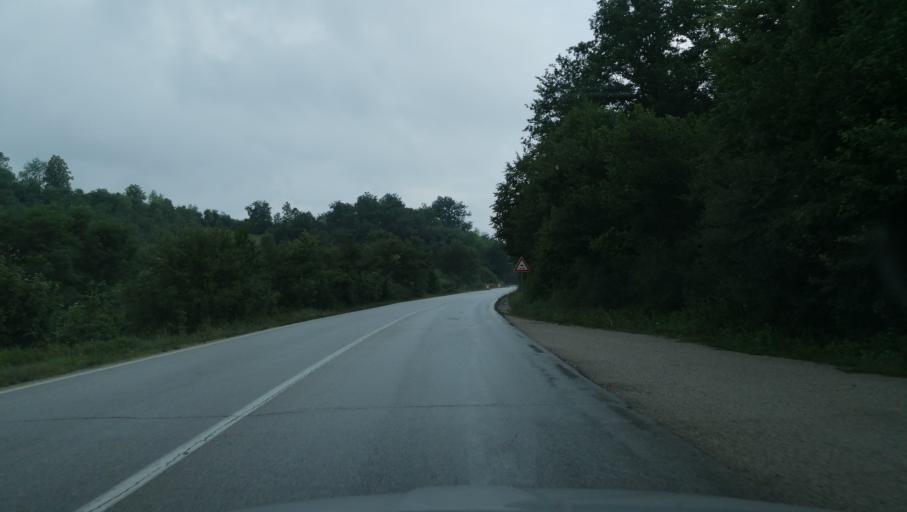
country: RS
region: Central Serbia
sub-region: Zlatiborski Okrug
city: Cajetina
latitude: 43.7894
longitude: 19.7136
